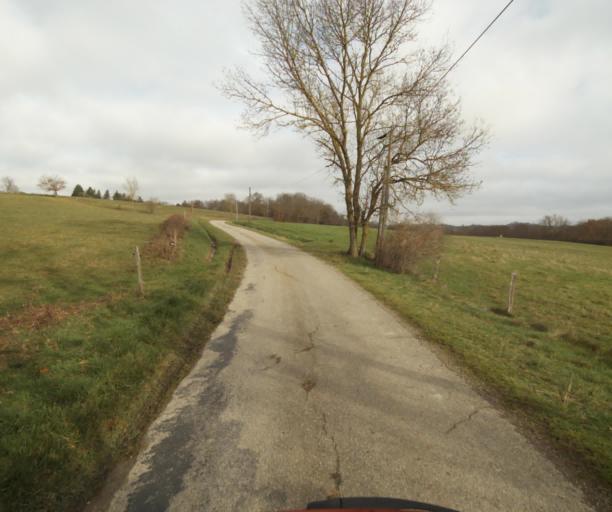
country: FR
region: Midi-Pyrenees
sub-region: Departement de la Haute-Garonne
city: Gaillac-Toulza
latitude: 43.1604
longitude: 1.4849
